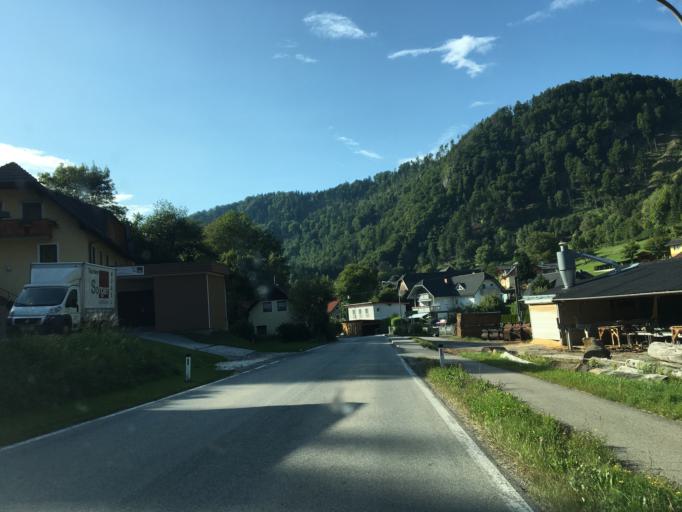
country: AT
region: Carinthia
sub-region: Politischer Bezirk Sankt Veit an der Glan
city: Bruckl
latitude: 46.7236
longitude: 14.5498
